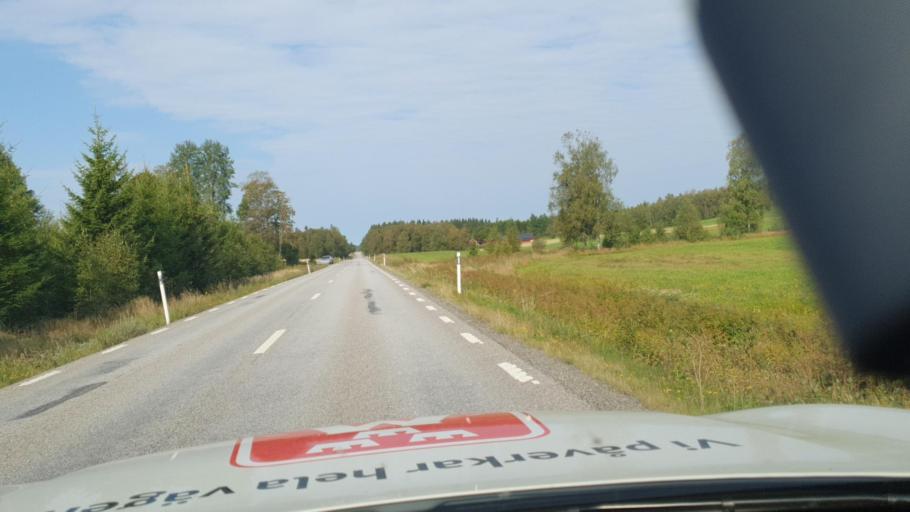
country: SE
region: Vaestra Goetaland
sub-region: Dals-Ed Kommun
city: Ed
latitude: 58.8686
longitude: 12.0230
